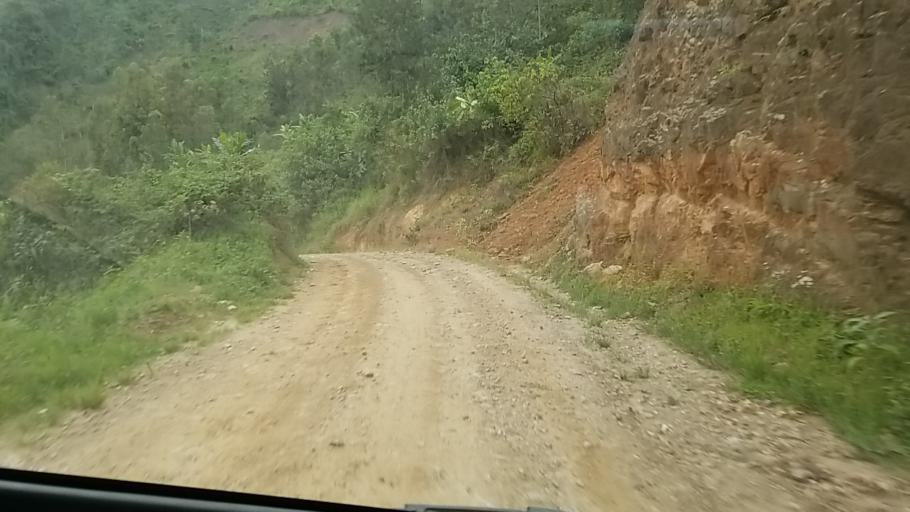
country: CD
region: Nord Kivu
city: Sake
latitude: -1.9645
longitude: 28.9156
